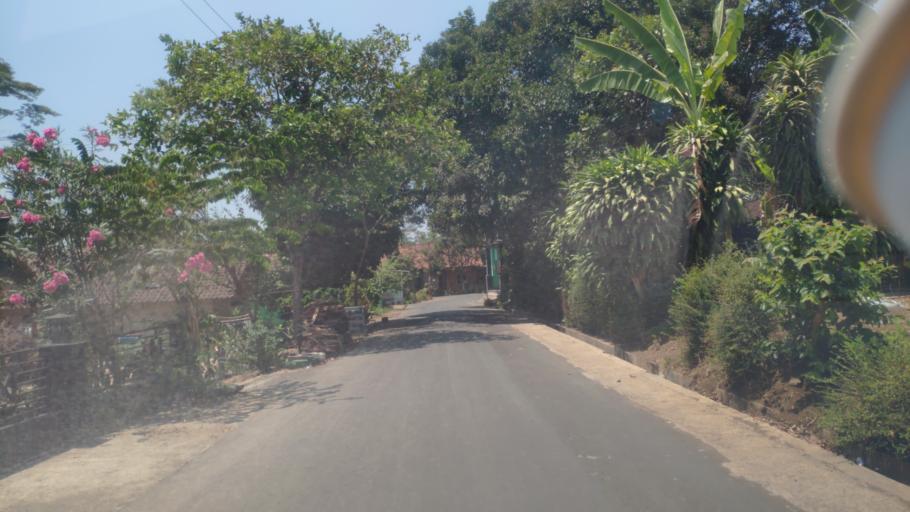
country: ID
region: Central Java
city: Wonosobo
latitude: -7.4049
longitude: 109.6750
